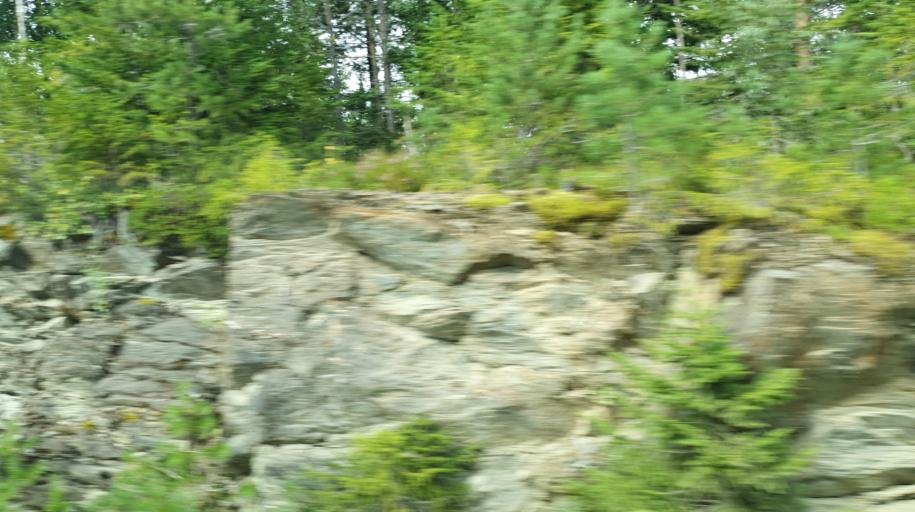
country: NO
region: Nord-Trondelag
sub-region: Levanger
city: Skogn
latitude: 63.5753
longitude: 11.2226
